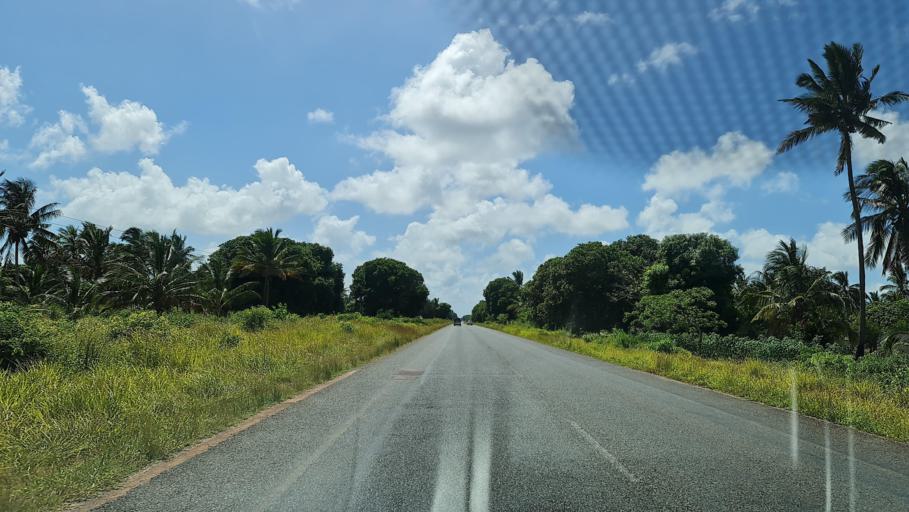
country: MZ
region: Inhambane
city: Maxixe
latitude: -24.5418
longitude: 34.9064
